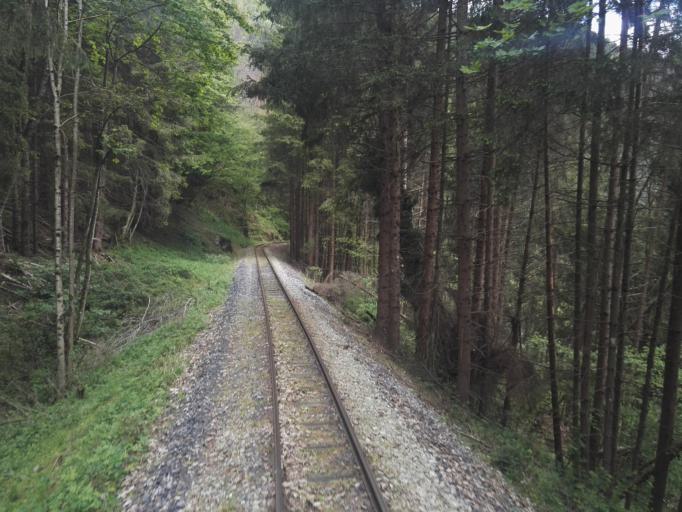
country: AT
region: Styria
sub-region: Politischer Bezirk Weiz
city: Birkfeld
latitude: 47.3340
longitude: 15.6982
